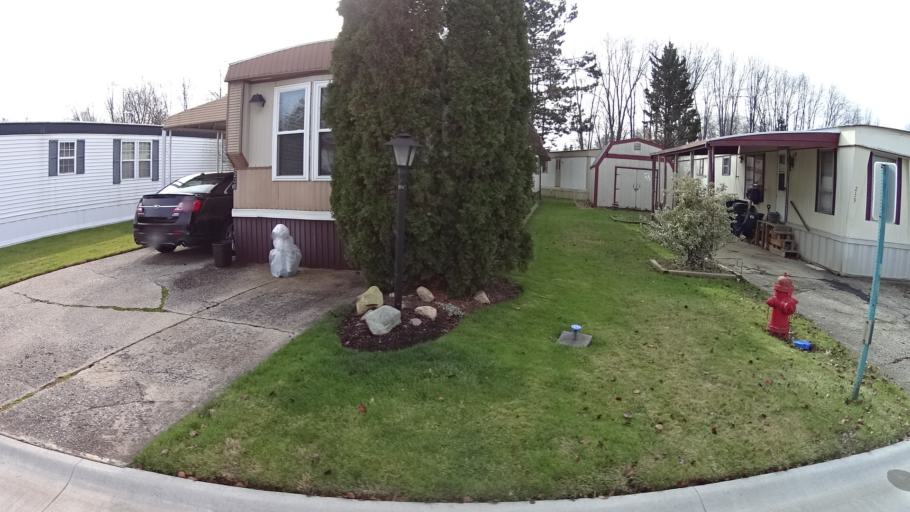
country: US
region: Ohio
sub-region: Lorain County
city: North Ridgeville
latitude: 41.3935
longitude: -81.9902
